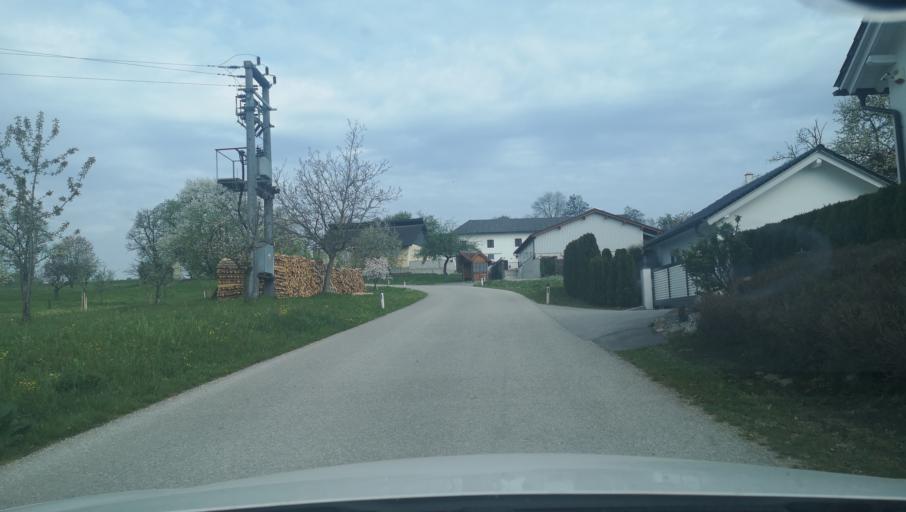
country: AT
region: Lower Austria
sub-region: Politischer Bezirk Melk
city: Blindenmarkt
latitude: 48.1336
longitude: 14.9712
